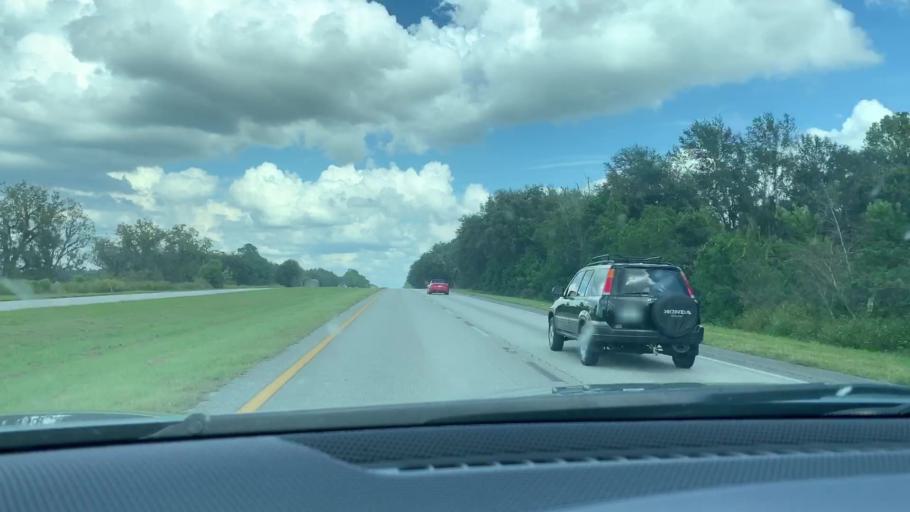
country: US
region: Florida
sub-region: Alachua County
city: Hawthorne
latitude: 29.6253
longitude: -82.0988
